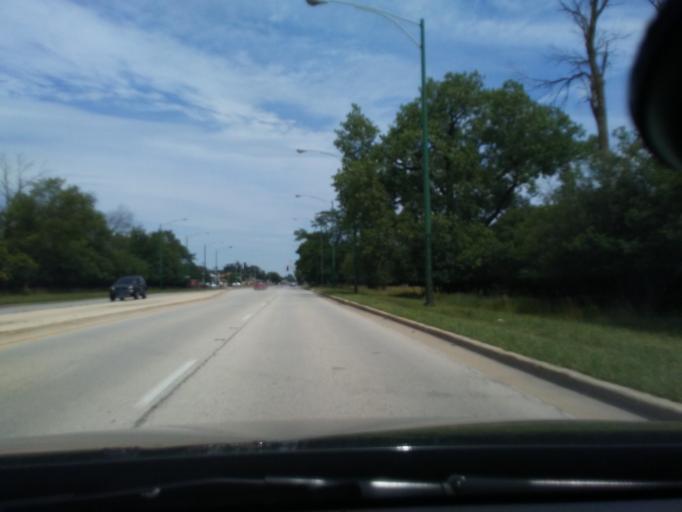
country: US
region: Illinois
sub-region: Cook County
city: Norridge
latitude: 41.9663
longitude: -87.8489
